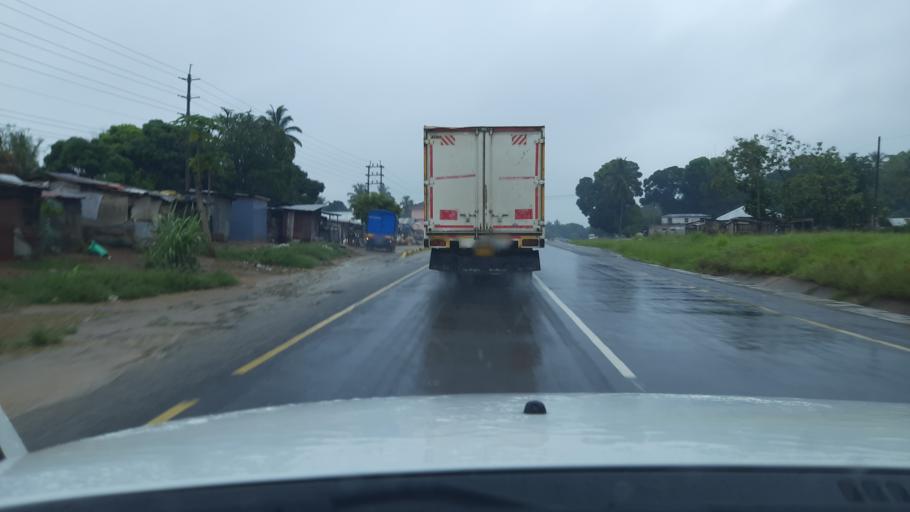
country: TZ
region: Pwani
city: Bagamoyo
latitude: -6.5814
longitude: 39.0332
